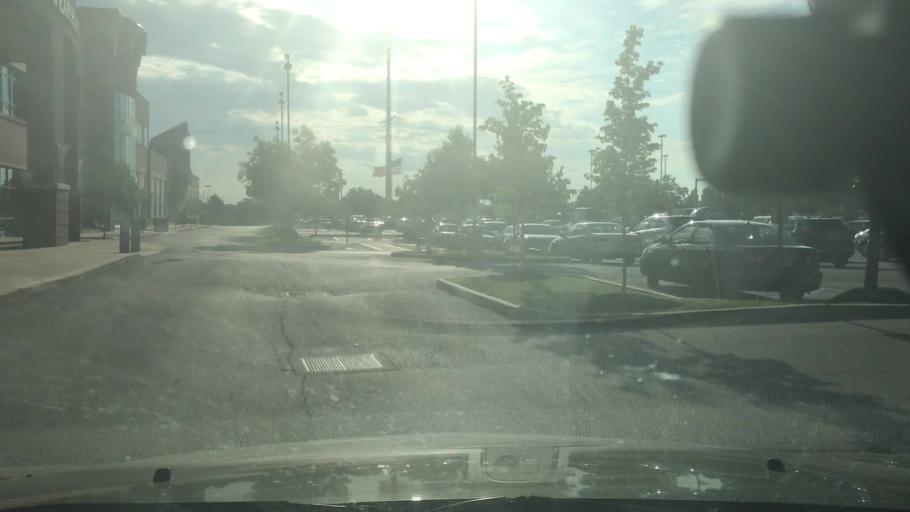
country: US
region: Missouri
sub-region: Saint Louis County
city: Richmond Heights
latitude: 38.6285
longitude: -90.3357
